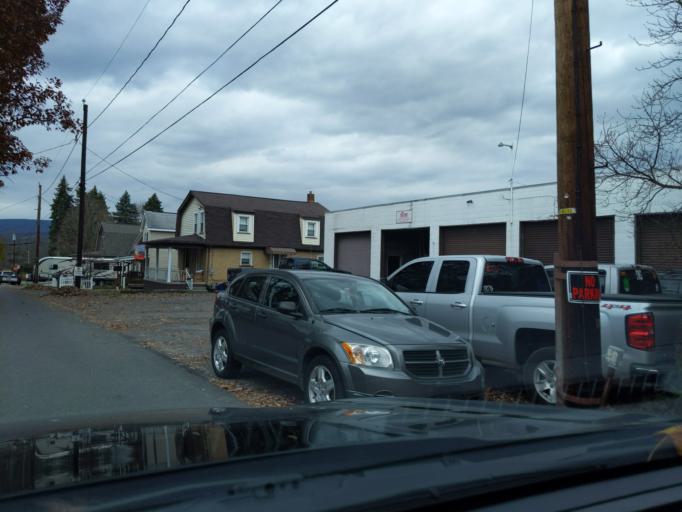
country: US
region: Pennsylvania
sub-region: Blair County
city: Greenwood
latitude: 40.5299
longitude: -78.3679
